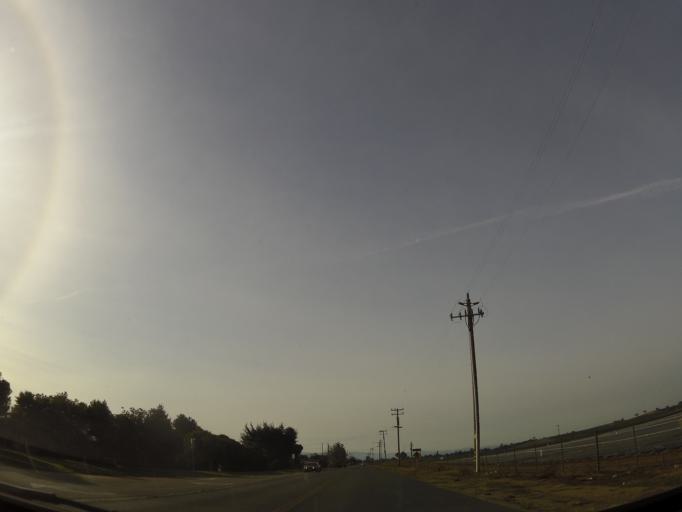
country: US
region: California
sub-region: Monterey County
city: Prunedale
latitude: 36.7614
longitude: -121.6142
